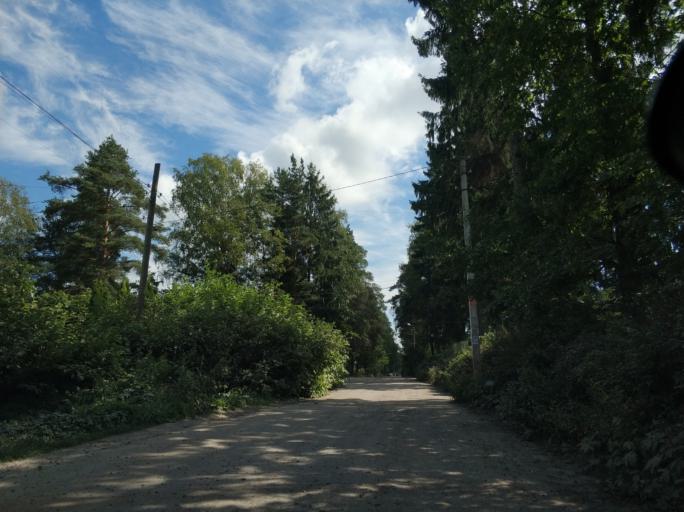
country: RU
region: Leningrad
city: Vsevolozhsk
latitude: 60.0200
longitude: 30.6155
